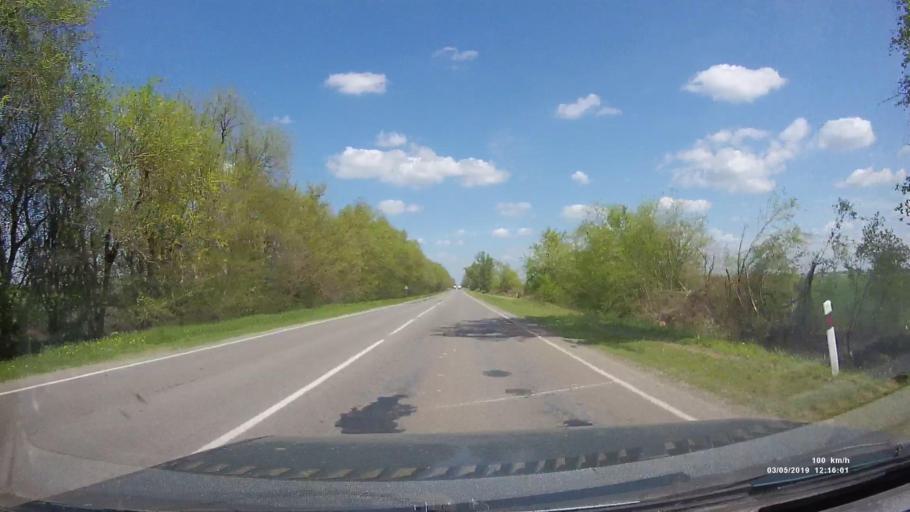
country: RU
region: Rostov
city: Melikhovskaya
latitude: 47.3659
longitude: 40.5797
